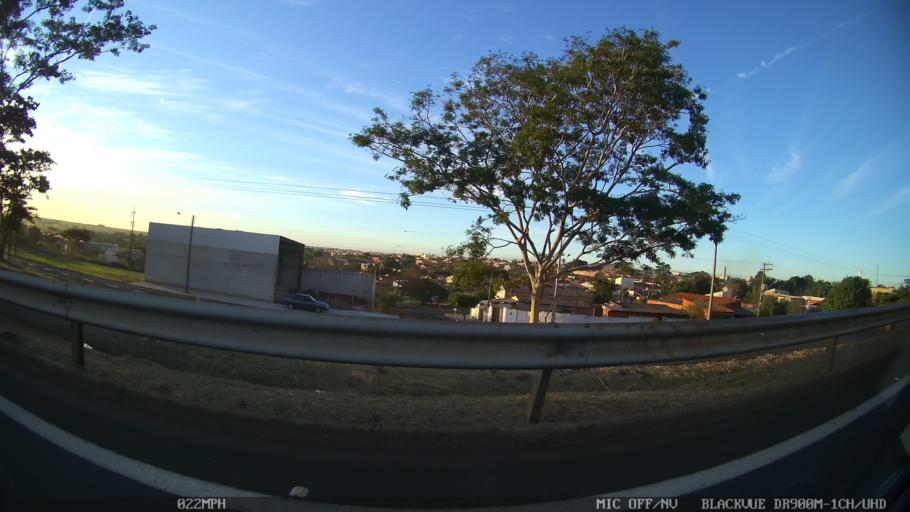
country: BR
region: Sao Paulo
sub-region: Catanduva
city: Catanduva
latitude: -21.1326
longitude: -49.0200
